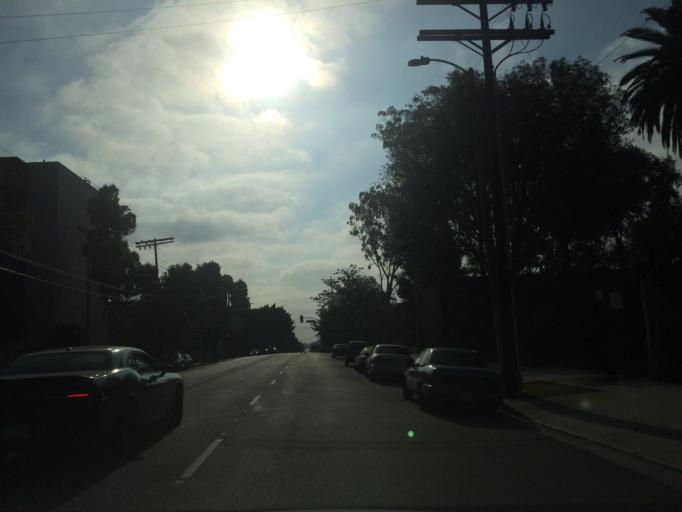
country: US
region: California
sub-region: Los Angeles County
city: View Park-Windsor Hills
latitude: 34.0326
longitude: -118.3125
